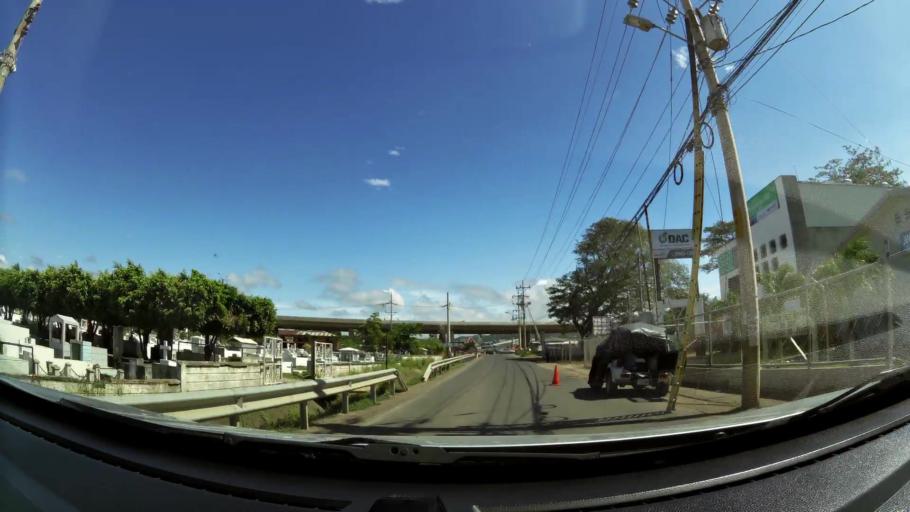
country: CR
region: Guanacaste
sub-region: Canton de Canas
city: Canas
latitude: 10.4256
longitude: -85.0949
